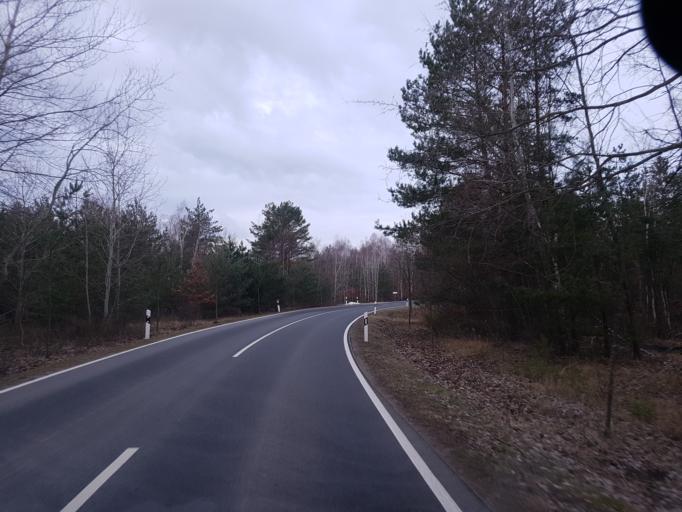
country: DE
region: Brandenburg
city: Sallgast
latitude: 51.5774
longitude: 13.8216
